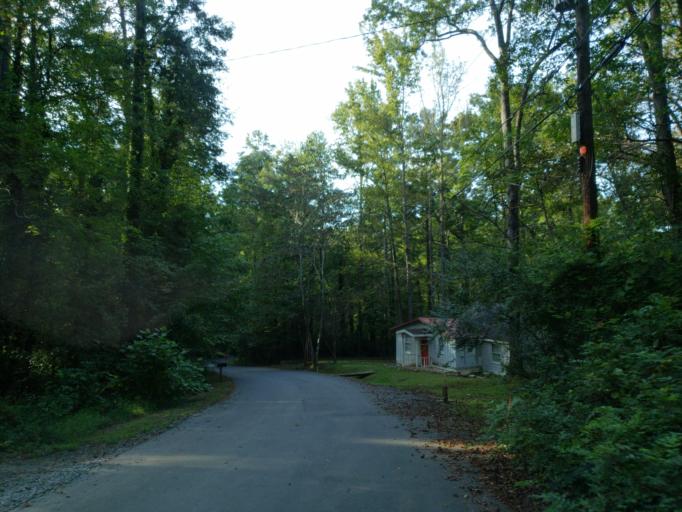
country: US
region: Georgia
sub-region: Fulton County
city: Roswell
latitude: 34.0797
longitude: -84.4164
